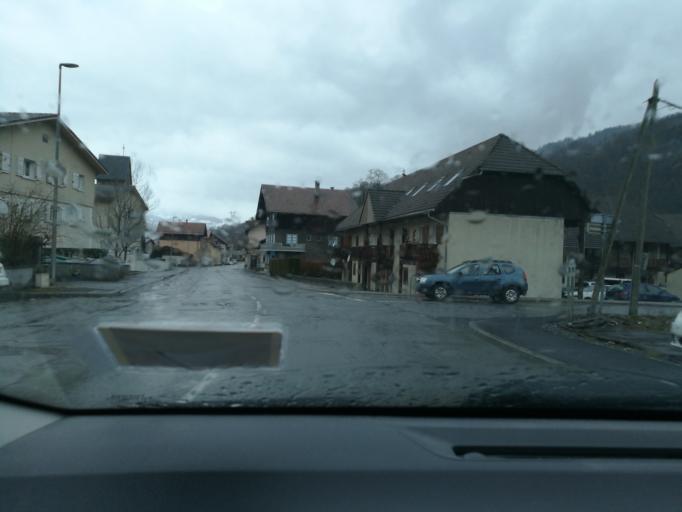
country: FR
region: Rhone-Alpes
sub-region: Departement de la Haute-Savoie
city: Saint-Gervais-les-Bains
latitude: 45.9281
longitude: 6.7239
